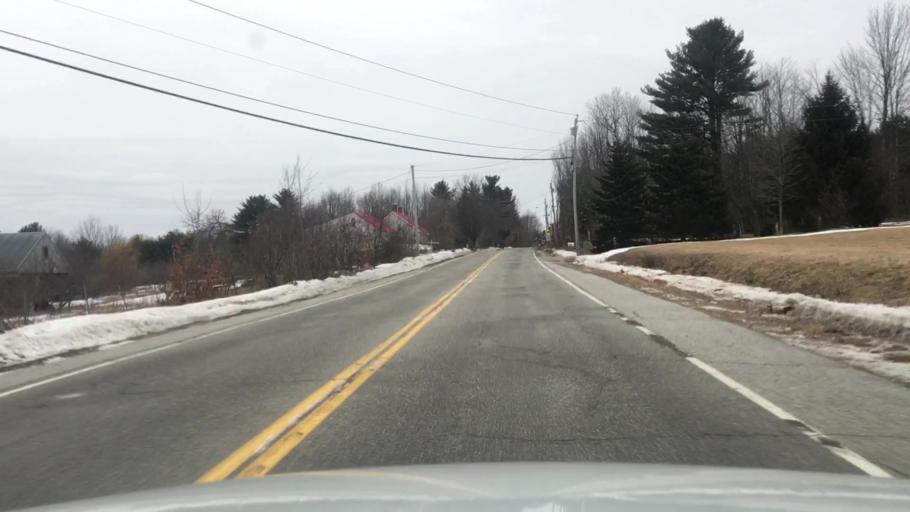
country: US
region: Maine
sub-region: York County
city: Shapleigh
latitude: 43.5304
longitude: -70.8506
